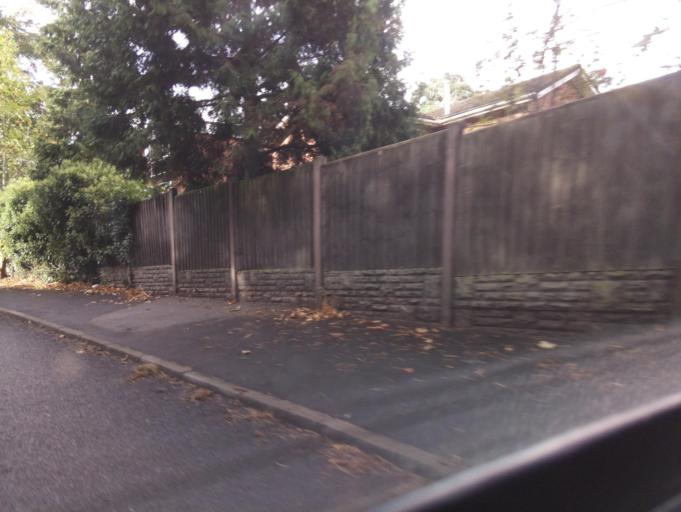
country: GB
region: England
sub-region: Worcestershire
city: Kidderminster
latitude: 52.3829
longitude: -2.2302
